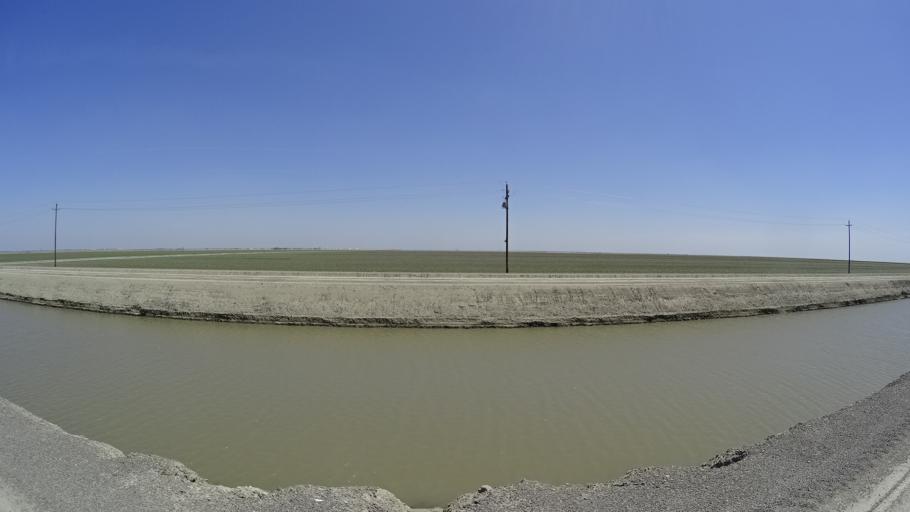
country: US
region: California
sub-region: Kings County
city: Corcoran
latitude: 36.0131
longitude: -119.6427
